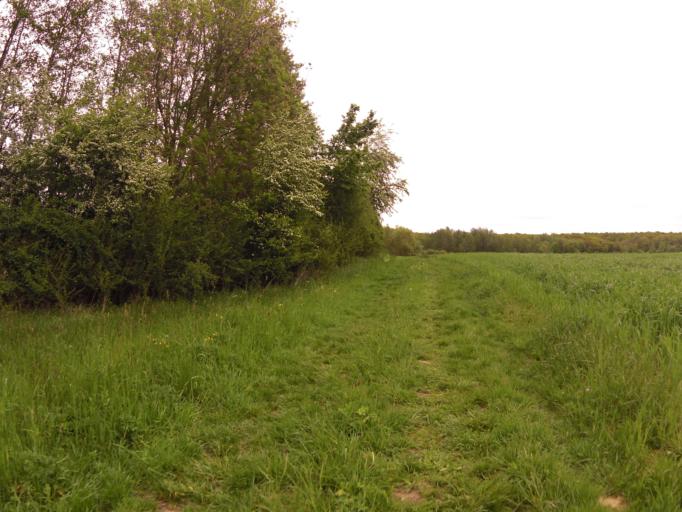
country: DE
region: Bavaria
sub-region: Regierungsbezirk Unterfranken
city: Kurnach
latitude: 49.8467
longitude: 10.0598
